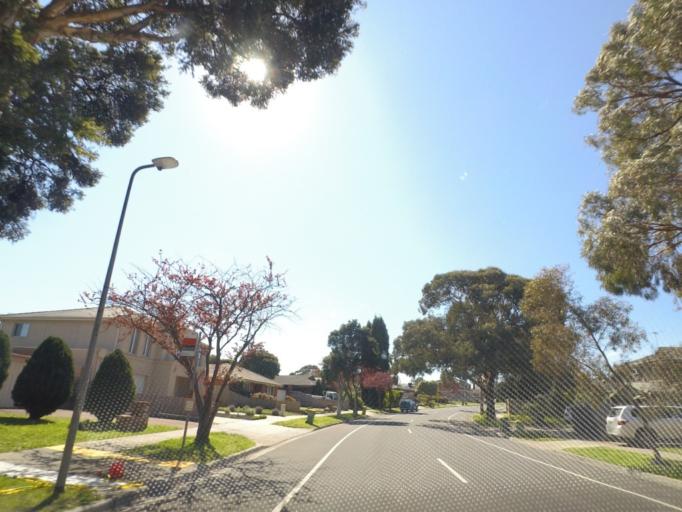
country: AU
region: Victoria
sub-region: Knox
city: Wantirna South
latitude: -37.8802
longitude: 145.2230
